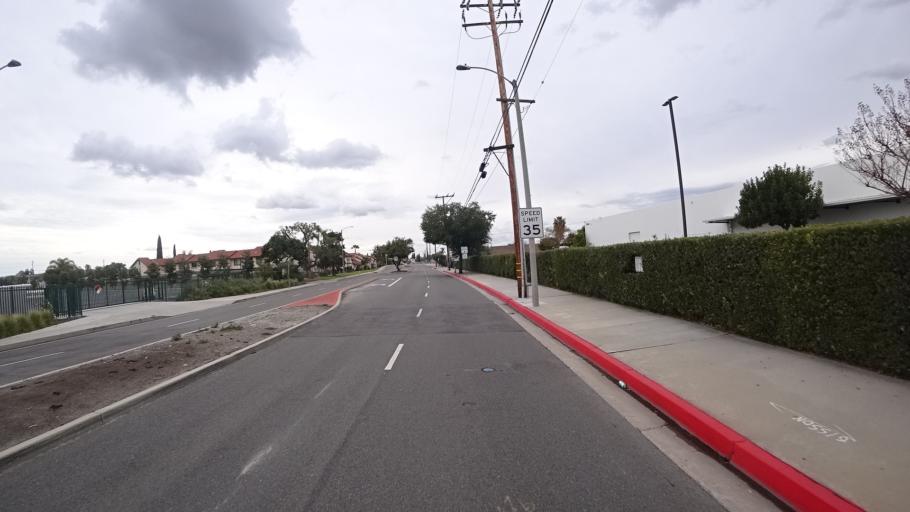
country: US
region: California
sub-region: Los Angeles County
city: Baldwin Park
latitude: 34.0902
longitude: -117.9453
